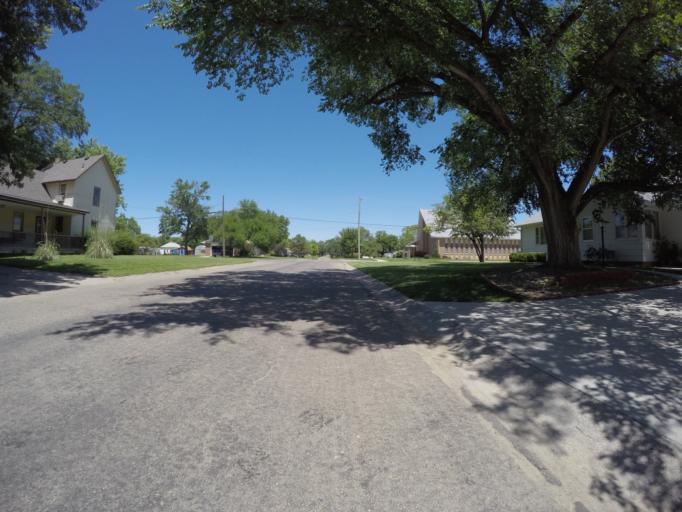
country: US
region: Kansas
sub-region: Republic County
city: Belleville
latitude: 39.8181
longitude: -97.6282
